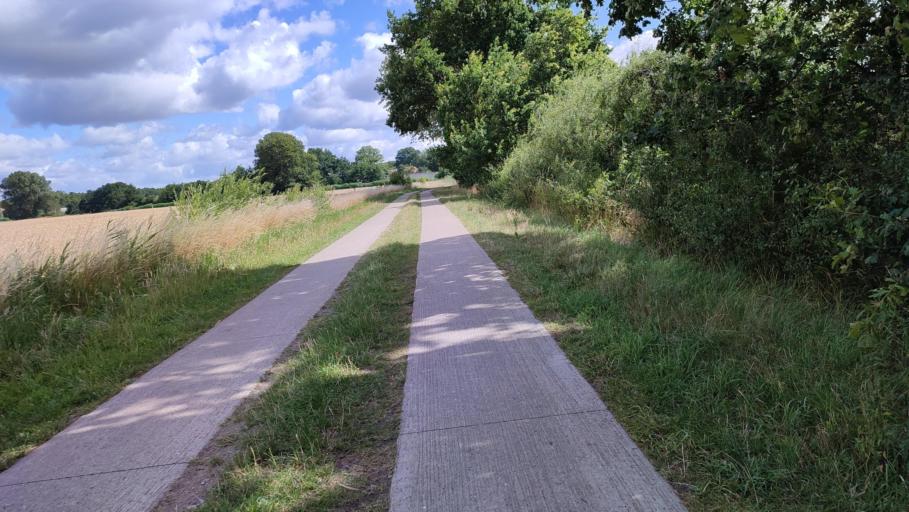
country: DE
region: Lower Saxony
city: Neu Darchau
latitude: 53.2243
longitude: 10.9790
